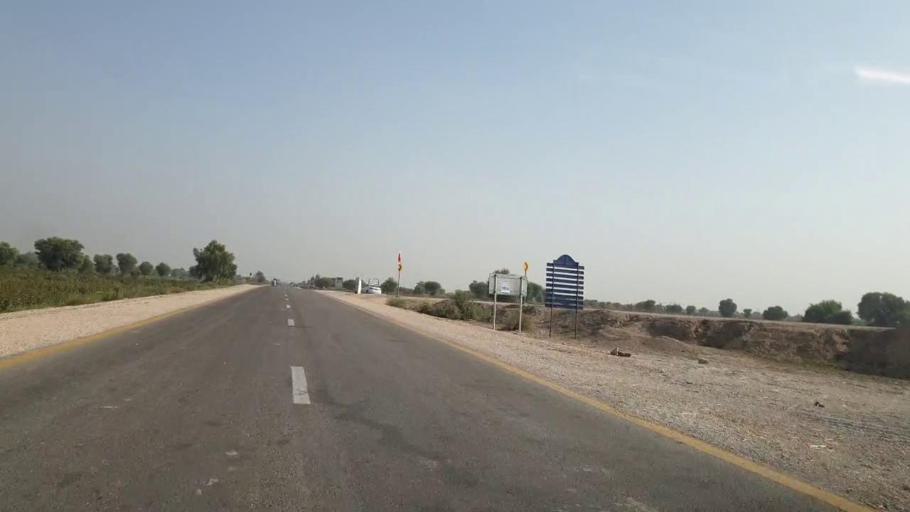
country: PK
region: Sindh
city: Sehwan
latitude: 26.4551
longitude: 67.8082
